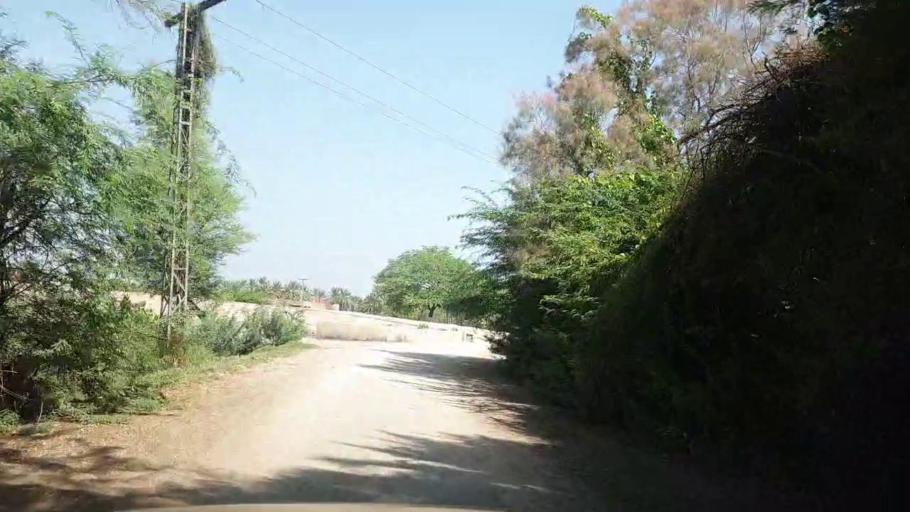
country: PK
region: Sindh
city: Rohri
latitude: 27.6916
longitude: 68.9488
